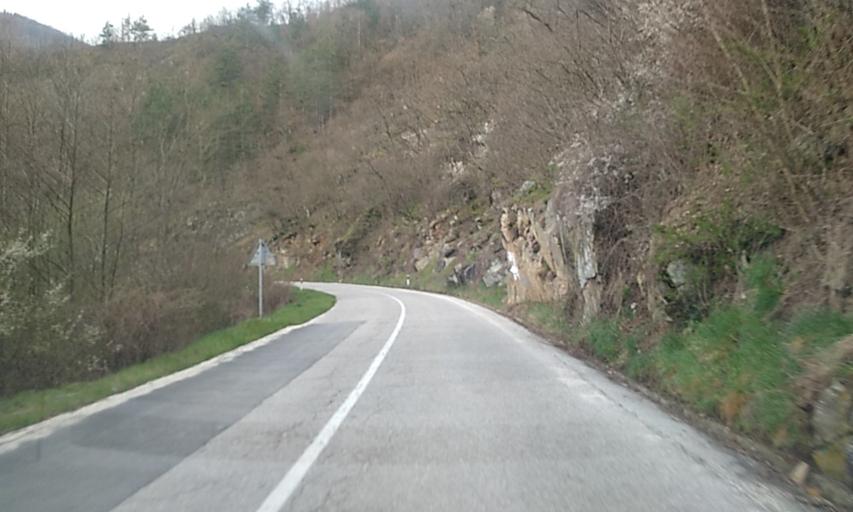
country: RS
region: Central Serbia
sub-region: Pcinjski Okrug
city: Bosilegrad
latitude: 42.5024
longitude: 22.4570
